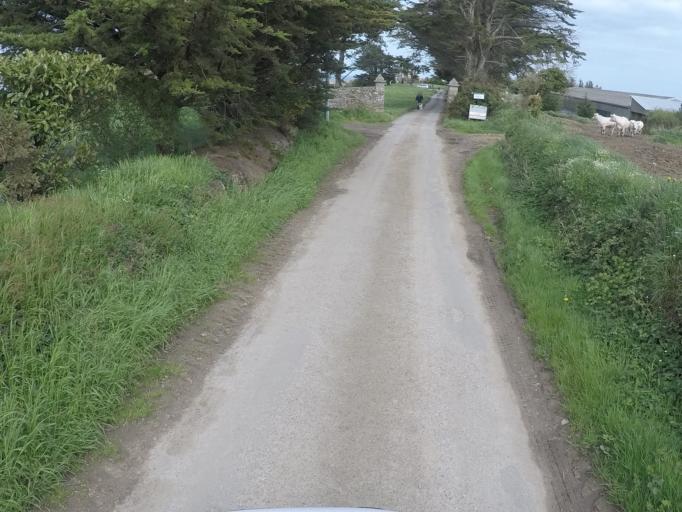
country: FR
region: Brittany
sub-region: Departement des Cotes-d'Armor
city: Plouha
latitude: 48.7133
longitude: -2.9362
